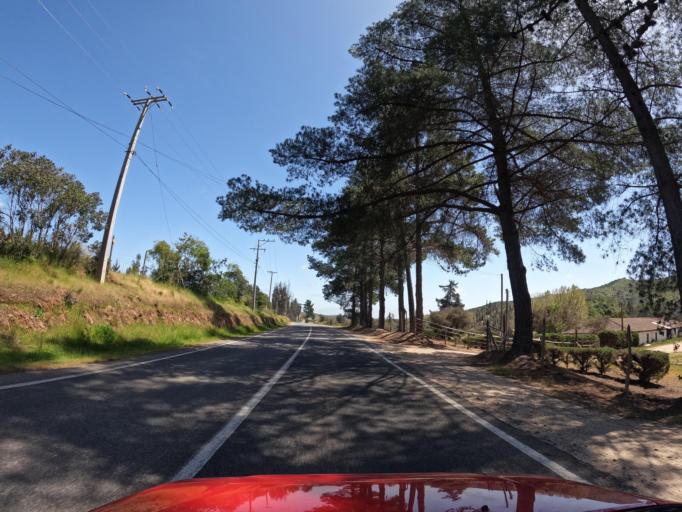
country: CL
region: O'Higgins
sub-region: Provincia de Colchagua
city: Santa Cruz
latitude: -34.6636
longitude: -71.8360
